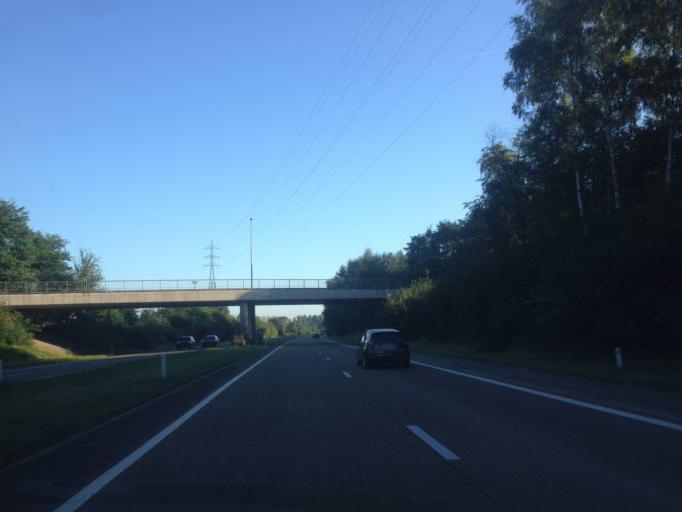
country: BE
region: Flanders
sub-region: Provincie Limburg
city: Overpelt
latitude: 51.1929
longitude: 5.3912
